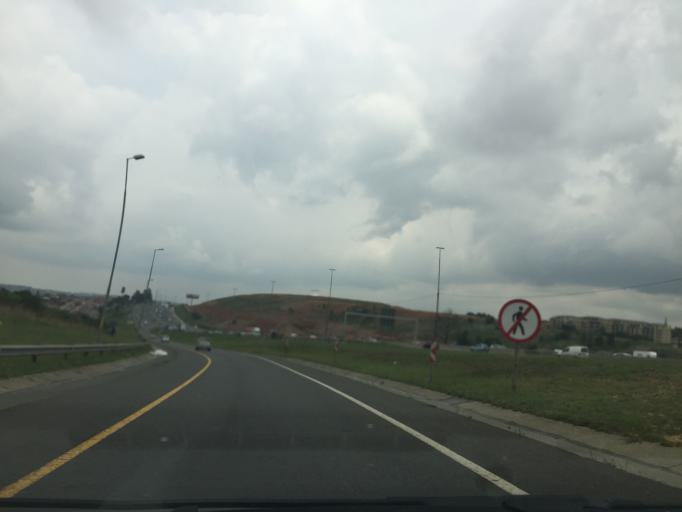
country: ZA
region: Gauteng
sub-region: City of Johannesburg Metropolitan Municipality
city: Modderfontein
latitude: -26.1035
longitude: 28.1231
